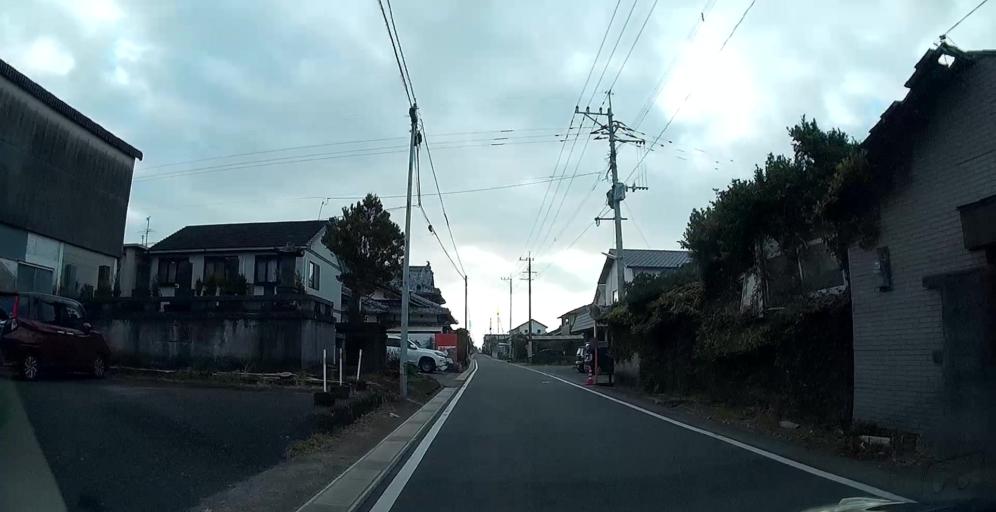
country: JP
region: Kumamoto
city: Yatsushiro
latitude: 32.5509
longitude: 130.6194
